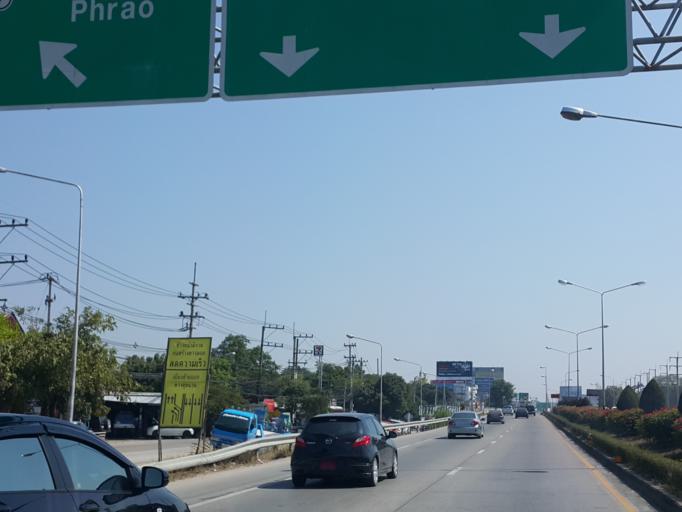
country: TH
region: Chiang Mai
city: Chiang Mai
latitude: 18.8111
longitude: 99.0000
